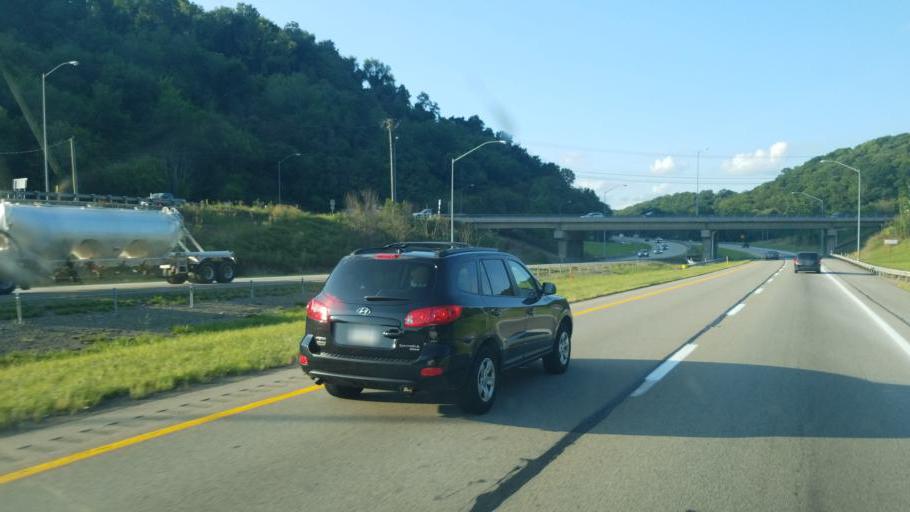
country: US
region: Pennsylvania
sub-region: Allegheny County
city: Franklin Park
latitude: 40.5514
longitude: -80.1182
